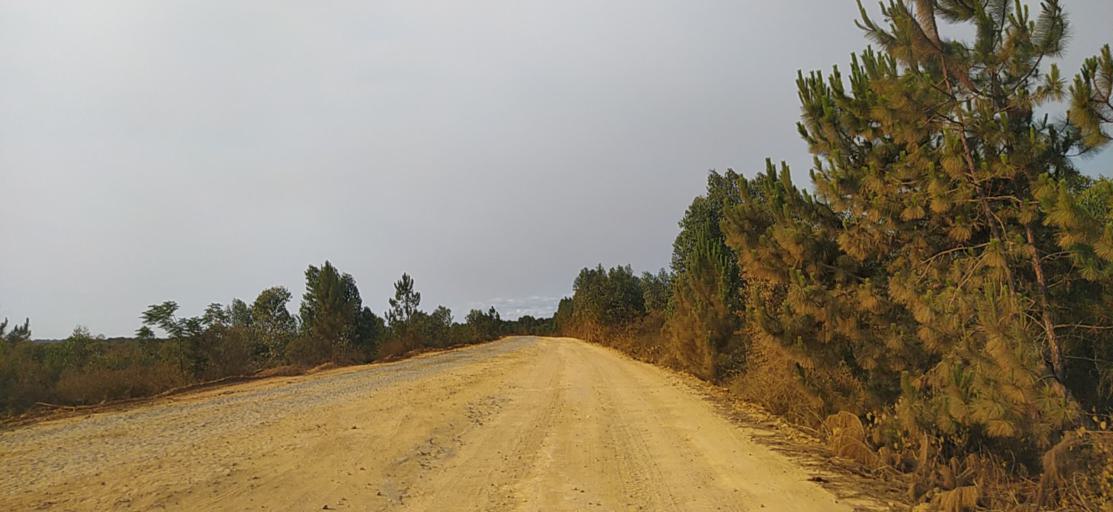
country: MG
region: Alaotra Mangoro
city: Moramanga
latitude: -18.6466
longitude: 48.2750
